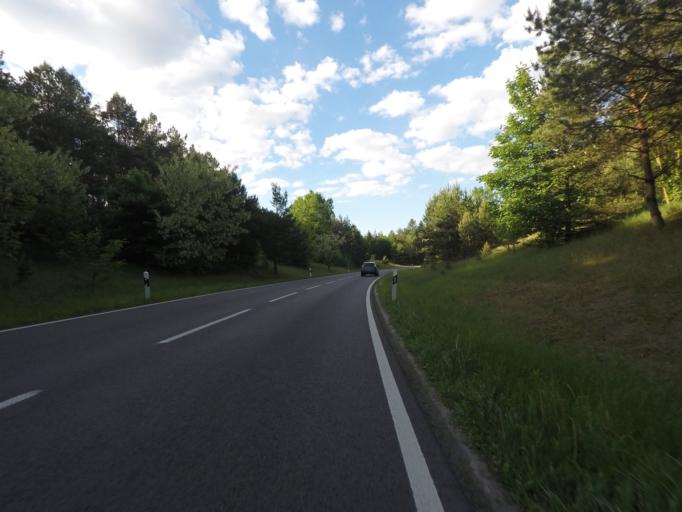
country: DE
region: Brandenburg
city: Britz
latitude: 52.8607
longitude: 13.7955
